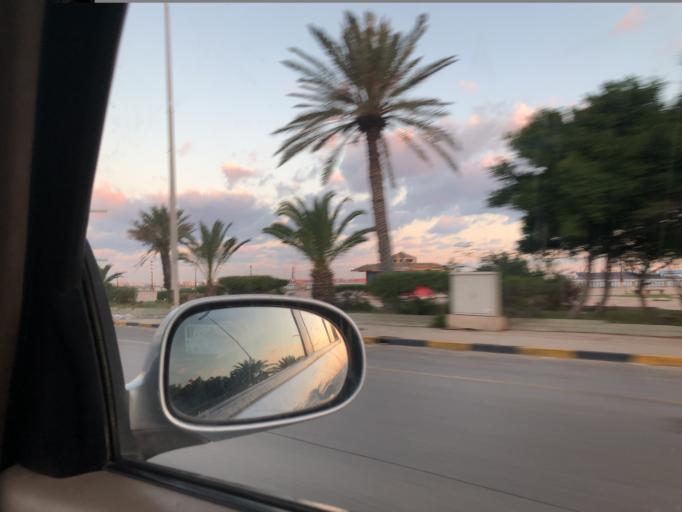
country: LY
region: Tripoli
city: Tripoli
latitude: 32.8949
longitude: 13.1874
